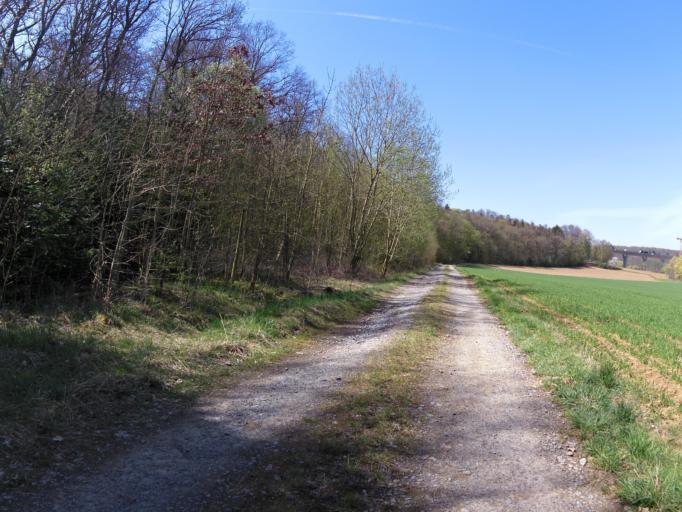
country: DE
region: Bavaria
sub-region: Regierungsbezirk Unterfranken
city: Estenfeld
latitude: 49.8556
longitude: 10.0027
